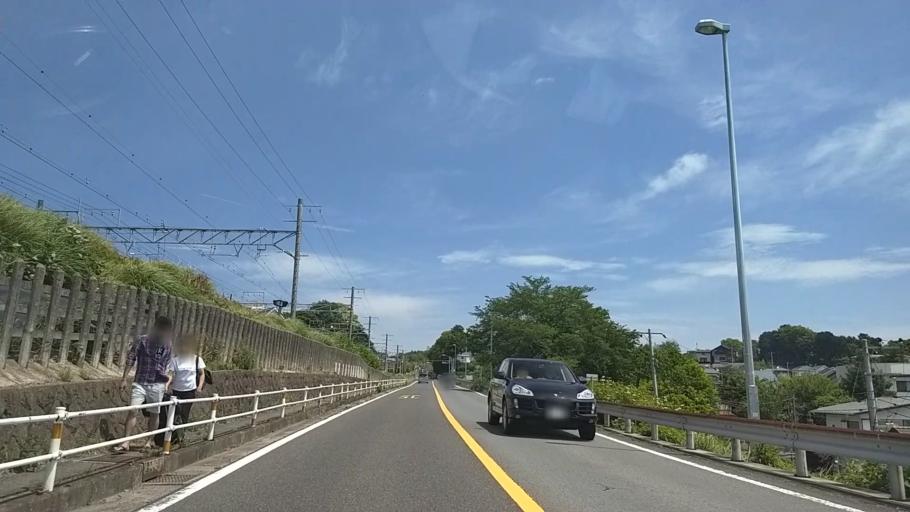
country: JP
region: Kanagawa
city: Yugawara
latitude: 35.1586
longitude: 139.1342
